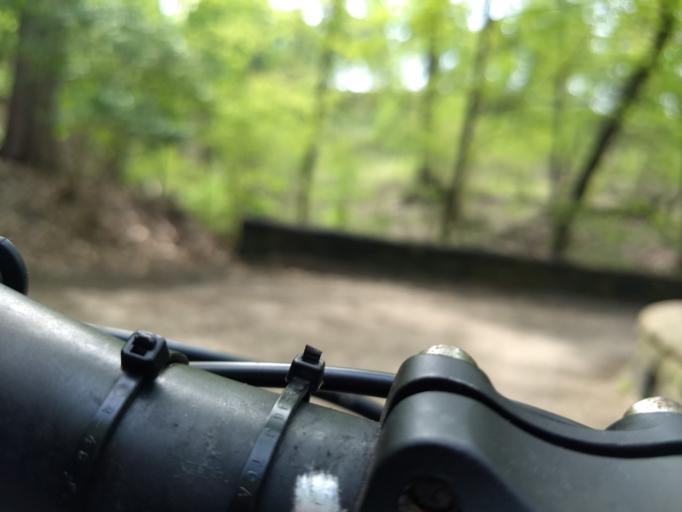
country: US
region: Pennsylvania
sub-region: Allegheny County
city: Bloomfield
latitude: 40.4332
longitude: -79.9476
